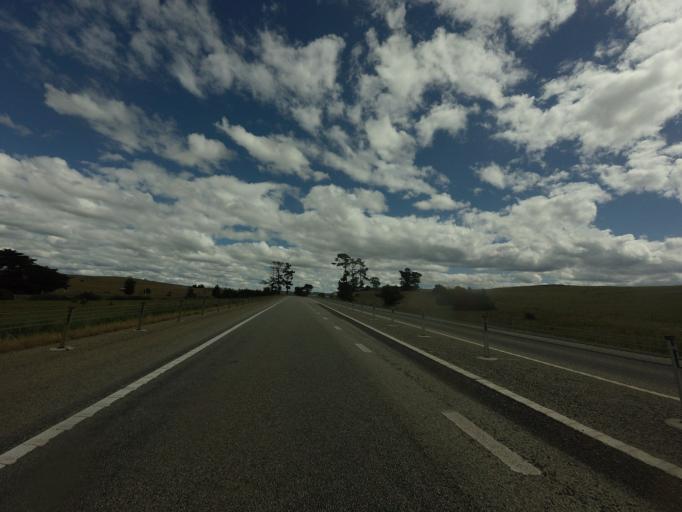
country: AU
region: Tasmania
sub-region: Northern Midlands
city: Evandale
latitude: -42.1444
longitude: 147.4178
